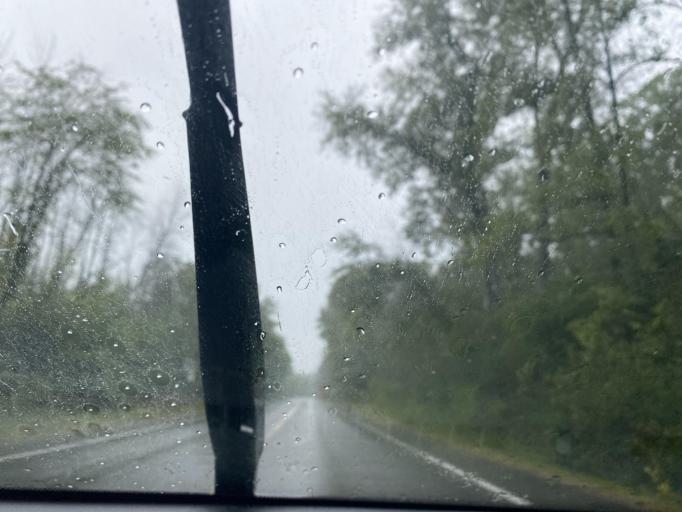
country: CA
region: Quebec
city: Baie-D'Urfe
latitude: 45.4488
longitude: -73.9305
